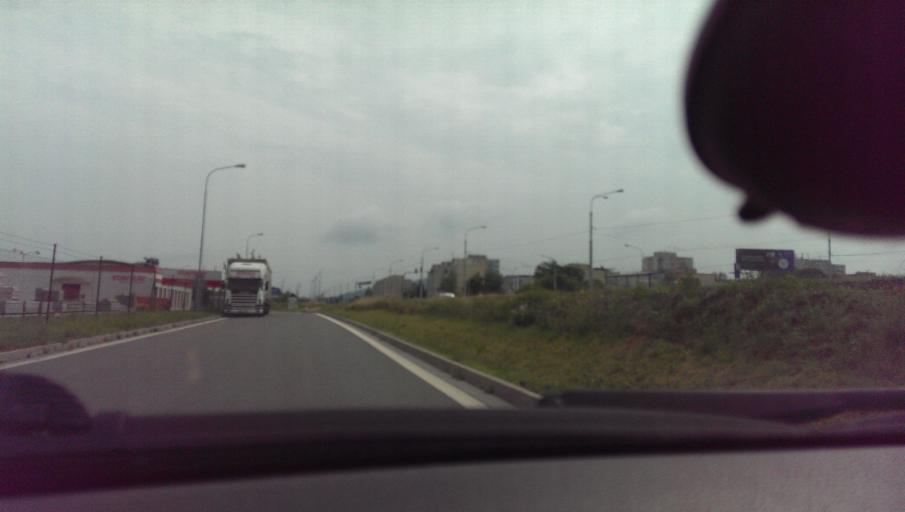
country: CZ
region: Zlin
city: Tecovice
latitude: 49.2063
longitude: 17.5775
